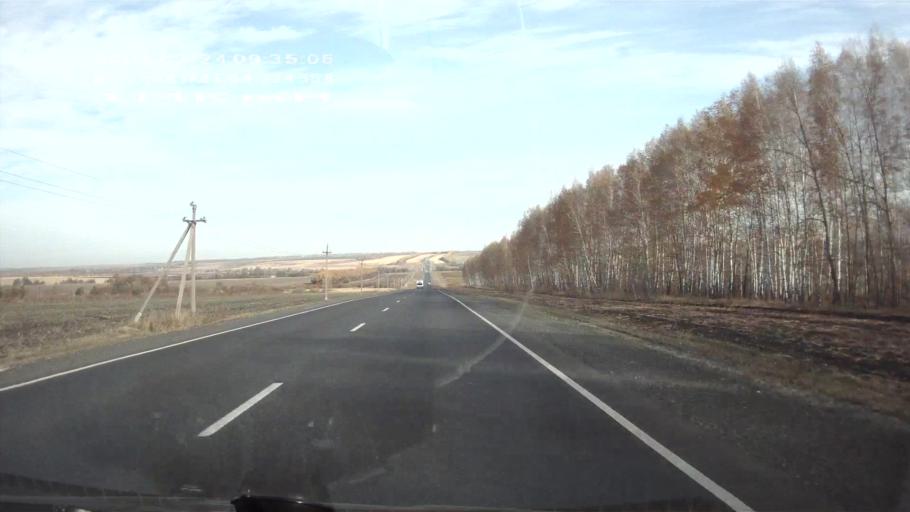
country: RU
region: Penza
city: Mokshan
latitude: 53.5982
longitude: 44.7246
